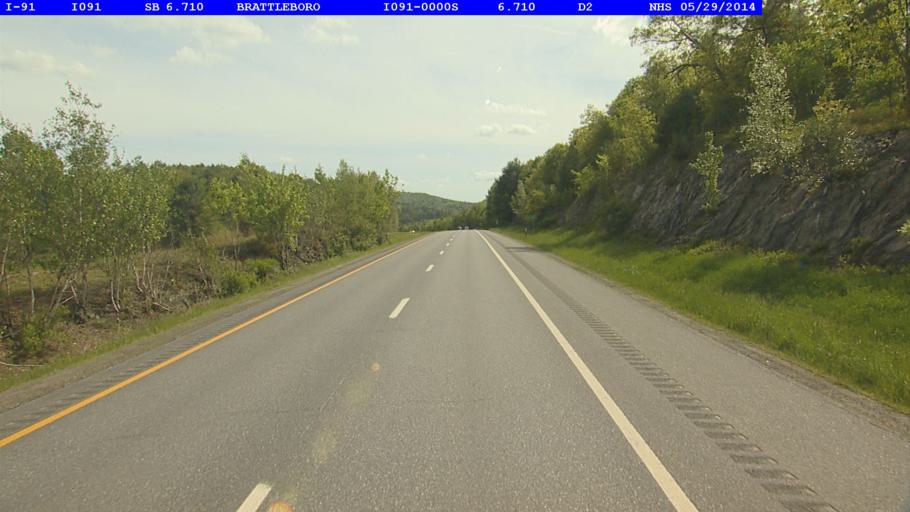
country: US
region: Vermont
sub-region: Windham County
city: Brattleboro
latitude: 42.8247
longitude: -72.5675
